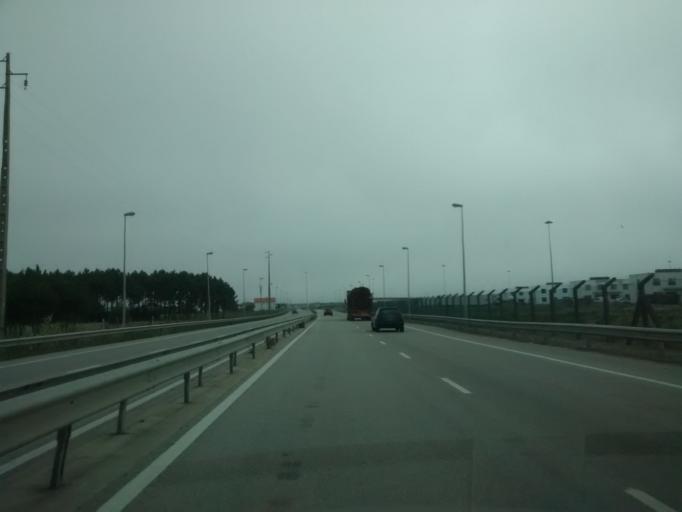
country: PT
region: Aveiro
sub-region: Ilhavo
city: Gafanha da Nazare
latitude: 40.6360
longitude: -8.7278
